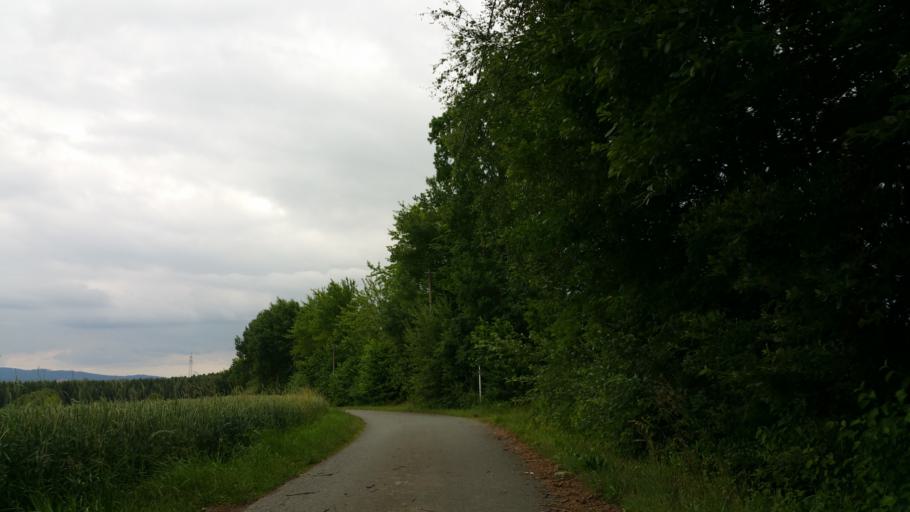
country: DE
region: Bavaria
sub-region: Upper Franconia
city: Schwarzenbach an der Saale
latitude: 50.2412
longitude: 11.9234
